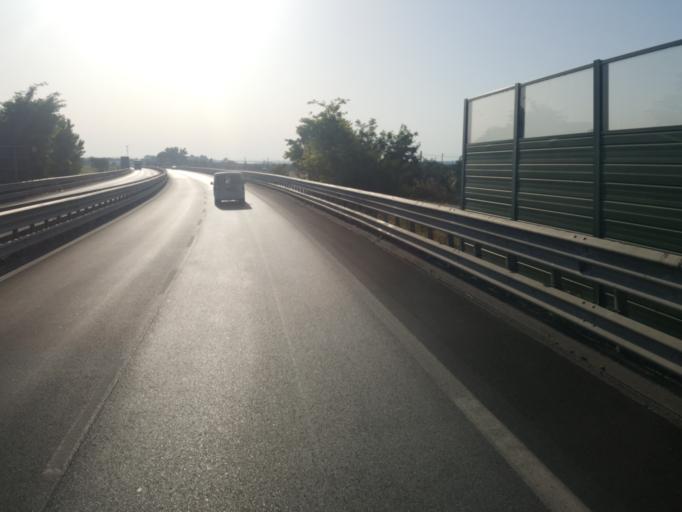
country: IT
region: Apulia
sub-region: Provincia di Foggia
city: Cerignola
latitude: 41.2633
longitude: 15.9276
